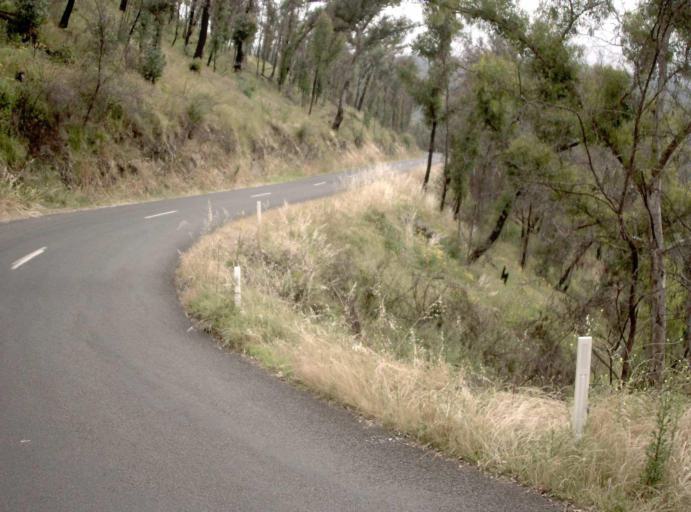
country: AU
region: Victoria
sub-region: Wellington
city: Heyfield
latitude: -37.8157
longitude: 146.6713
